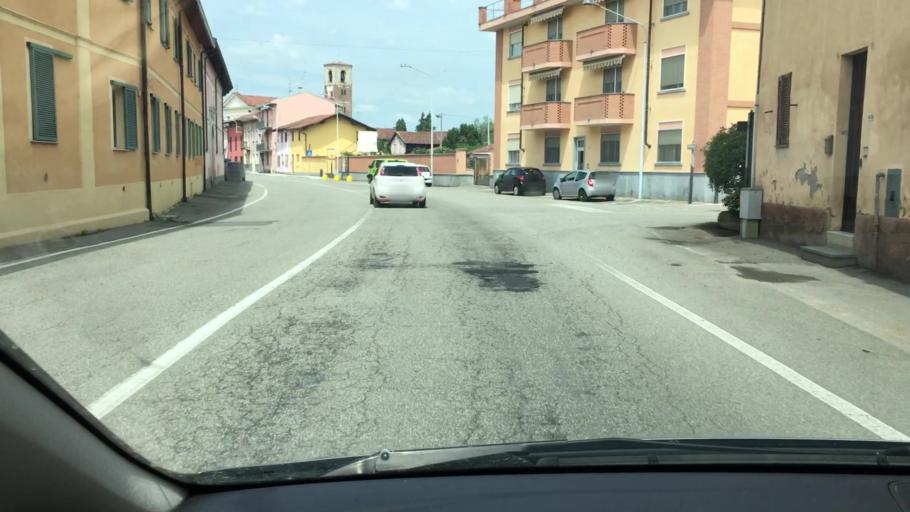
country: IT
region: Piedmont
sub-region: Provincia di Novara
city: Casalbeltrame
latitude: 45.4344
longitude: 8.4682
